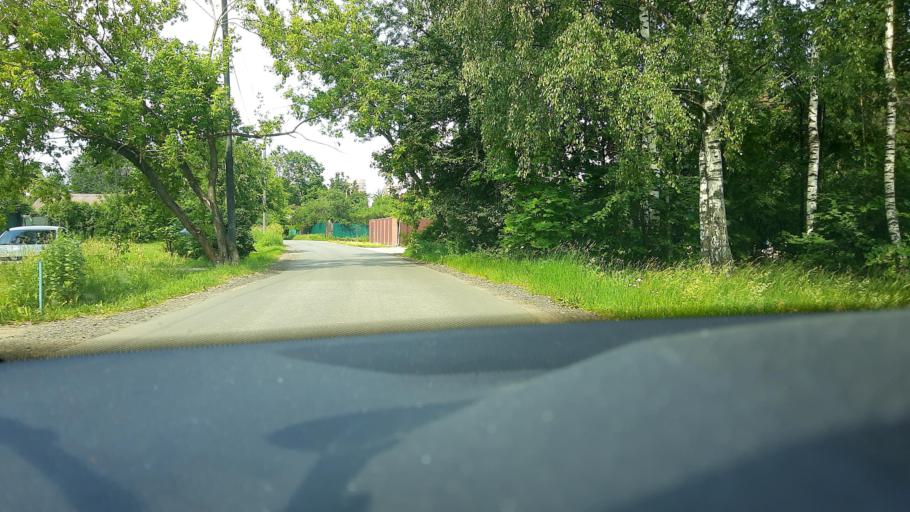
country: RU
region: Moscow
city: Strogino
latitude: 55.7833
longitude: 37.3972
